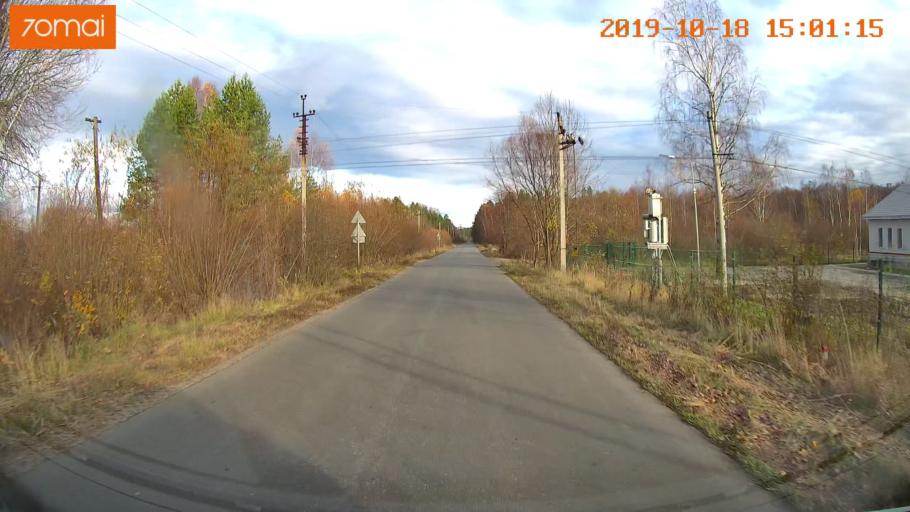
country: RU
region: Vladimir
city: Gus'-Khrustal'nyy
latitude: 55.4997
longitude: 40.5983
